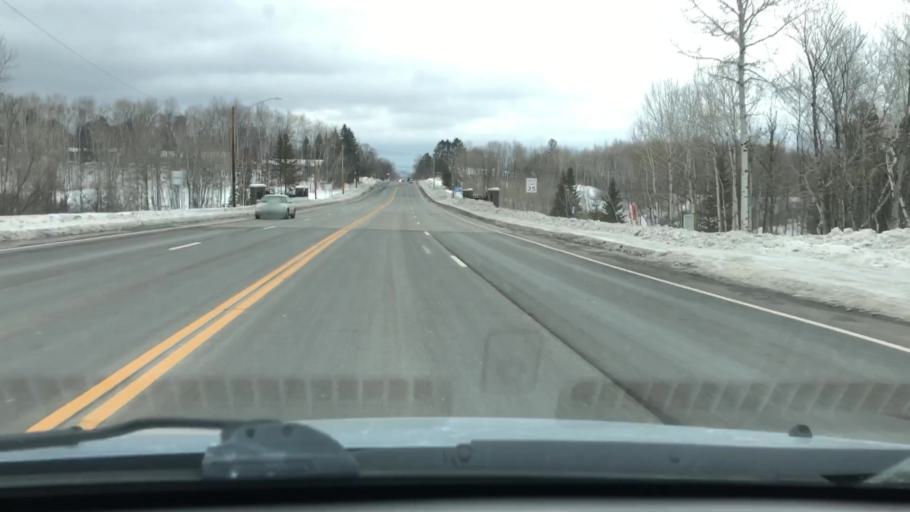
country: US
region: Minnesota
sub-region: Saint Louis County
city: Proctor
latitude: 46.7158
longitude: -92.2019
